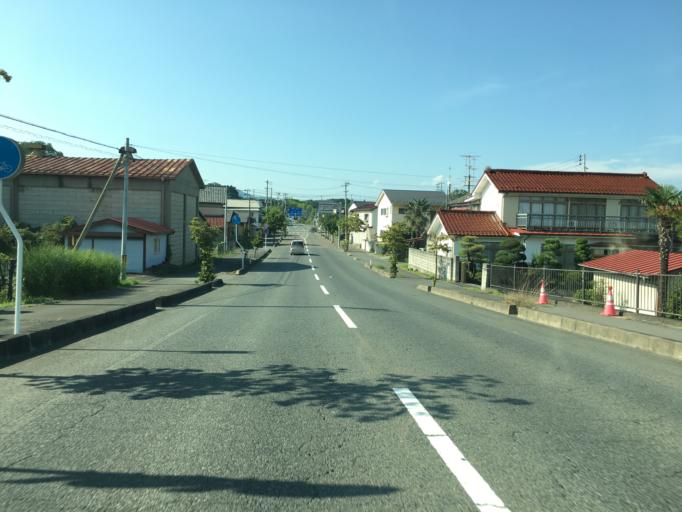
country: JP
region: Miyagi
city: Marumori
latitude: 37.7907
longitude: 140.9124
